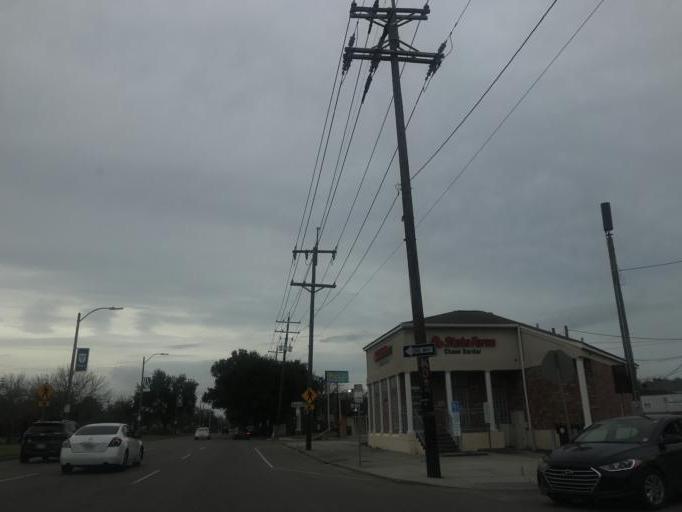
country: US
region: Louisiana
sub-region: Orleans Parish
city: New Orleans
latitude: 29.9463
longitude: -90.1137
